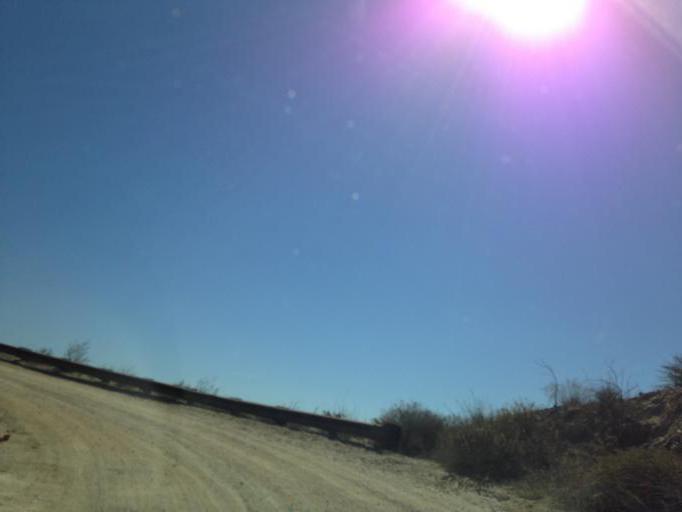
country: US
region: California
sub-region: San Bernardino County
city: Mentone
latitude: 34.1118
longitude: -117.1233
